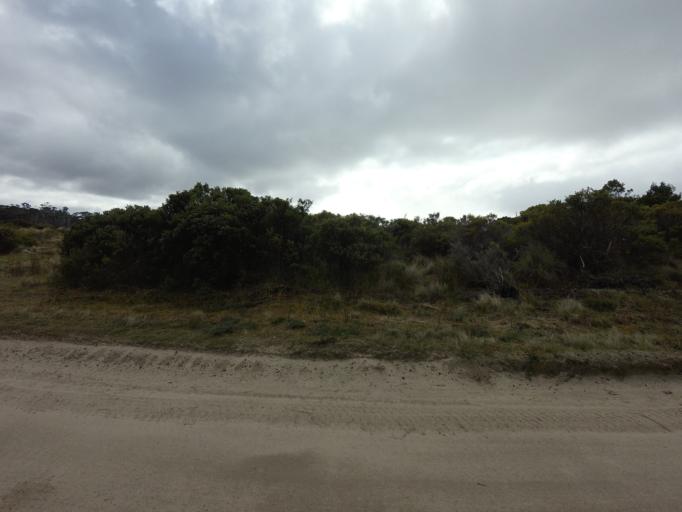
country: AU
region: Tasmania
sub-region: Huon Valley
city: Geeveston
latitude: -43.5801
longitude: 146.8879
